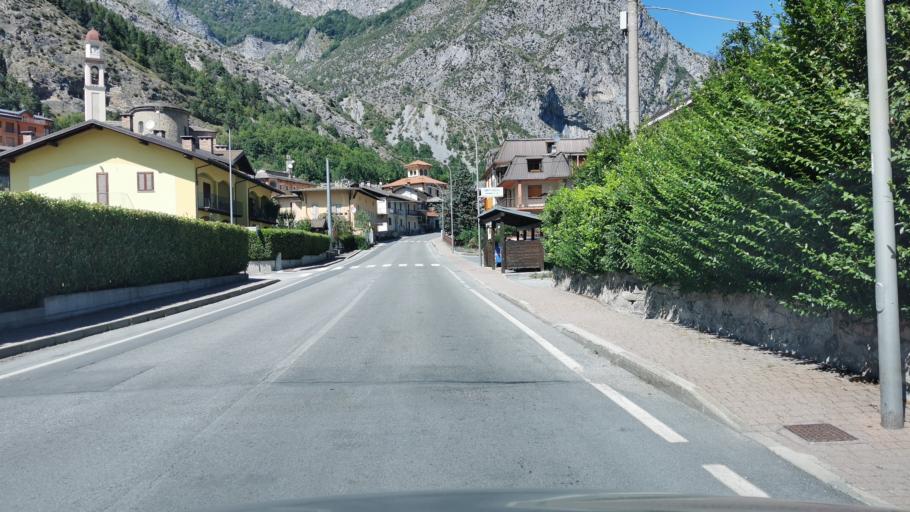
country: IT
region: Piedmont
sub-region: Provincia di Cuneo
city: Valdieri
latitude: 44.2752
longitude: 7.3968
